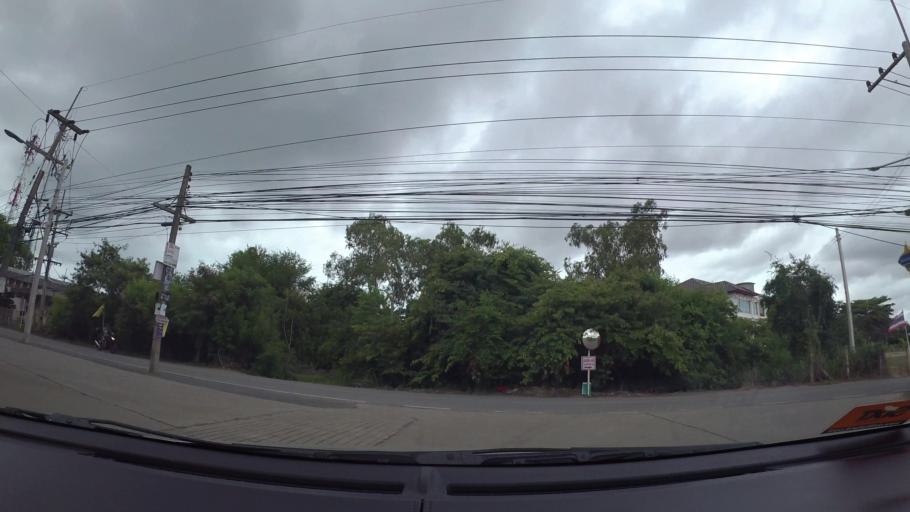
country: TH
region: Chon Buri
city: Sattahip
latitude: 12.7276
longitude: 100.8937
